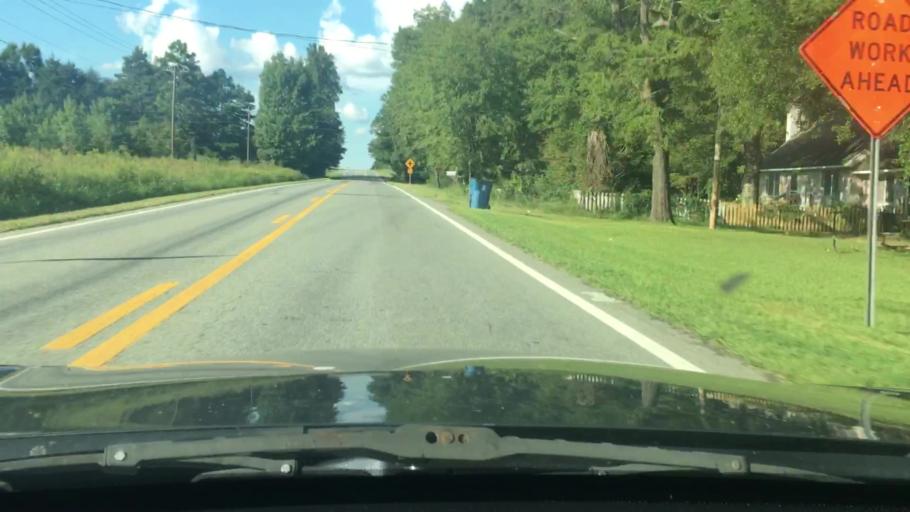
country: US
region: North Carolina
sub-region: Alamance County
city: Green Level
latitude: 36.1654
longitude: -79.3332
